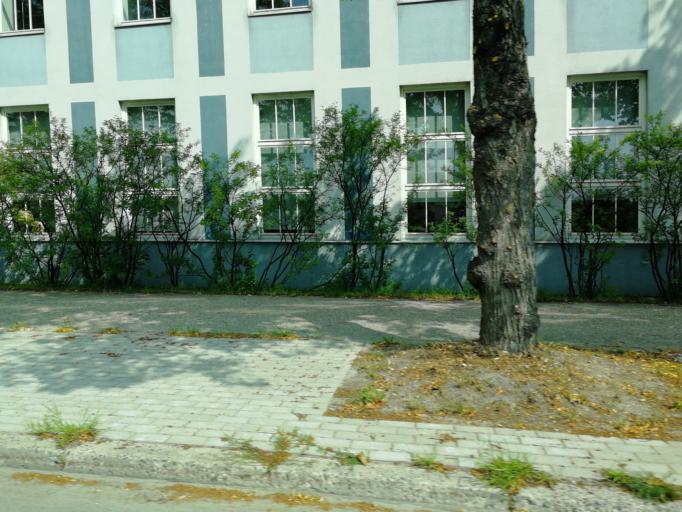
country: EE
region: Paernumaa
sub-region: Paernu linn
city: Parnu
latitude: 58.3919
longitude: 24.5072
